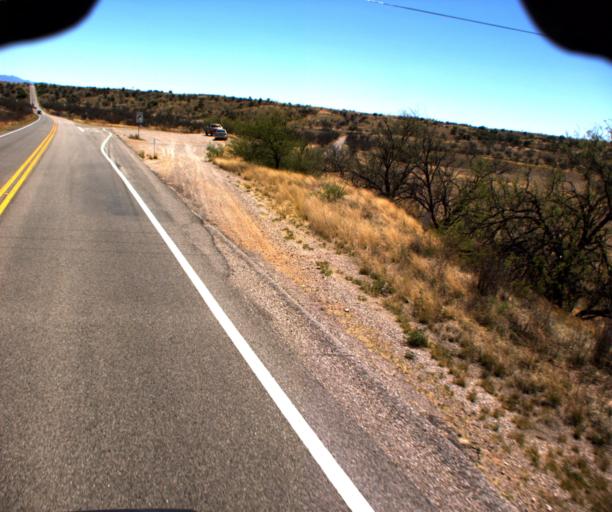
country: US
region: Arizona
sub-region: Pima County
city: Corona de Tucson
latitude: 31.7863
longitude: -110.6969
